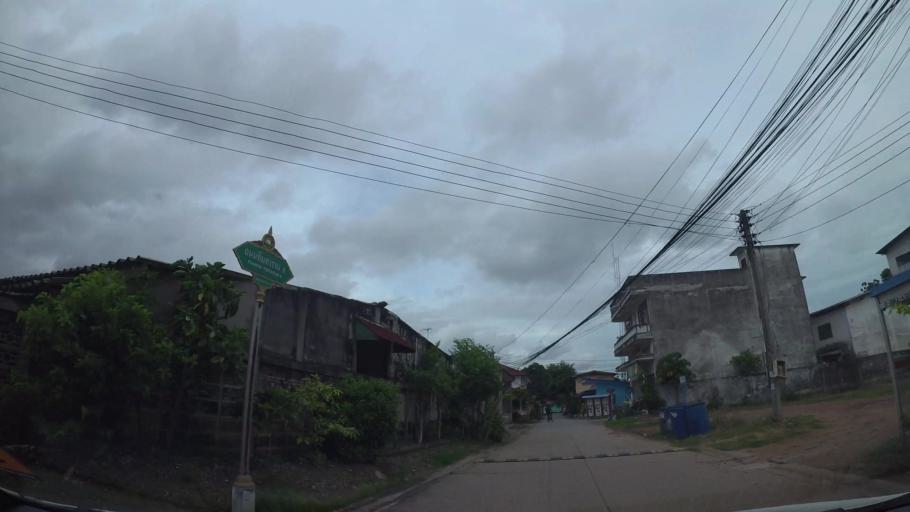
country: TH
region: Rayong
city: Rayong
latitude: 12.6770
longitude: 101.2655
